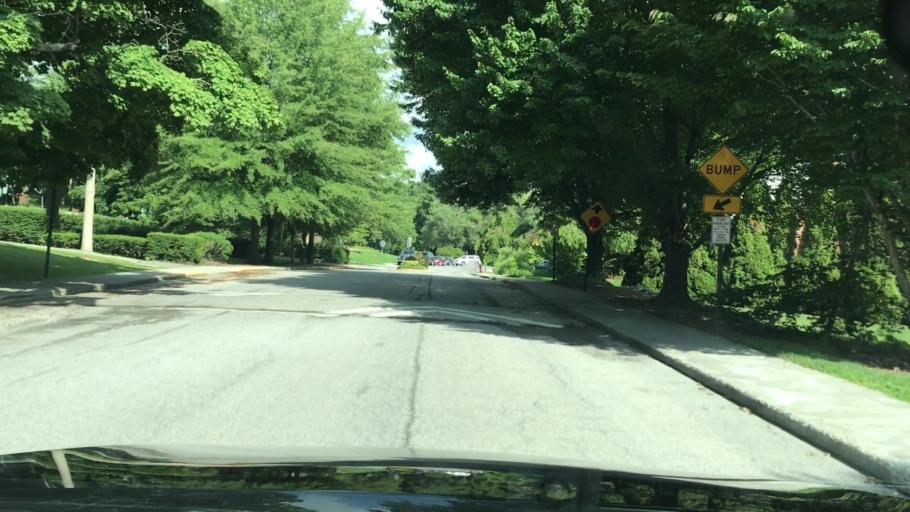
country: US
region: Virginia
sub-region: Montgomery County
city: Blacksburg
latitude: 37.2254
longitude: -80.4114
